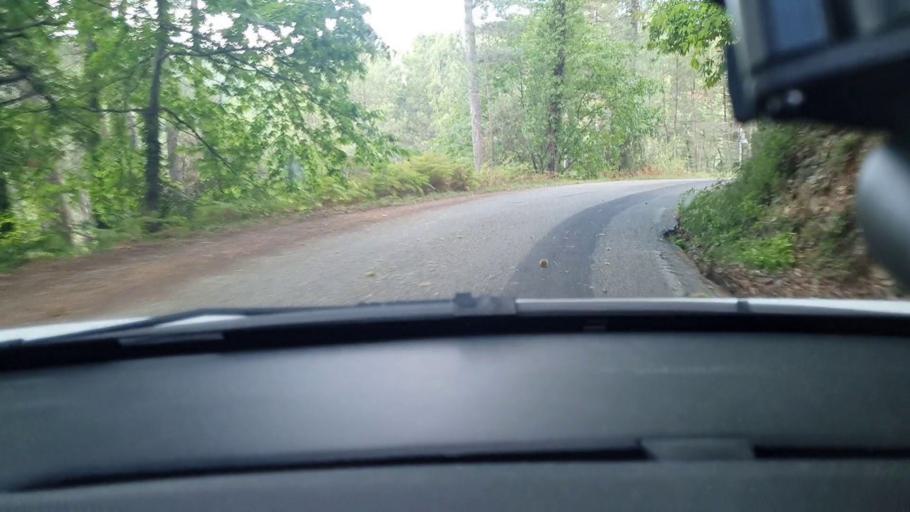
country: FR
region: Languedoc-Roussillon
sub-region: Departement du Gard
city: Besseges
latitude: 44.3277
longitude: 4.0033
